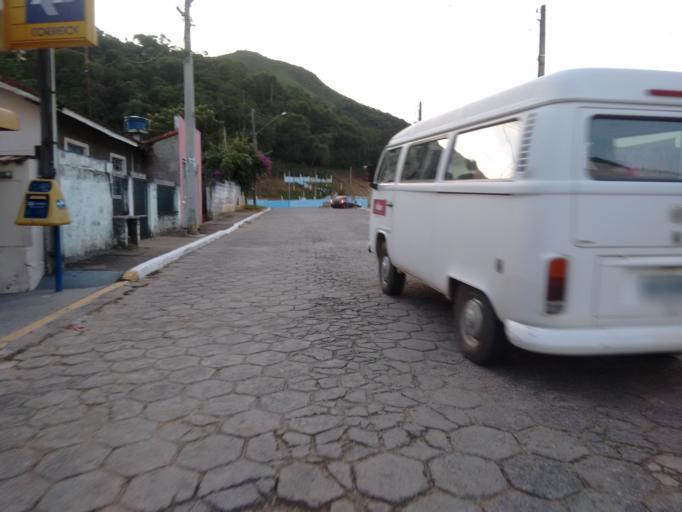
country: BR
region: Sao Paulo
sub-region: Apiai
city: Apiai
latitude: -24.5868
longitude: -48.5960
